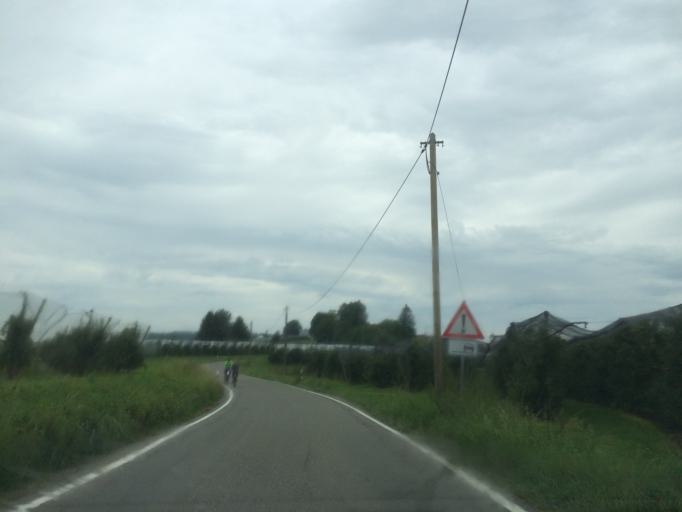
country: DE
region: Baden-Wuerttemberg
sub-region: Tuebingen Region
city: Hagnau
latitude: 47.6963
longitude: 9.3459
